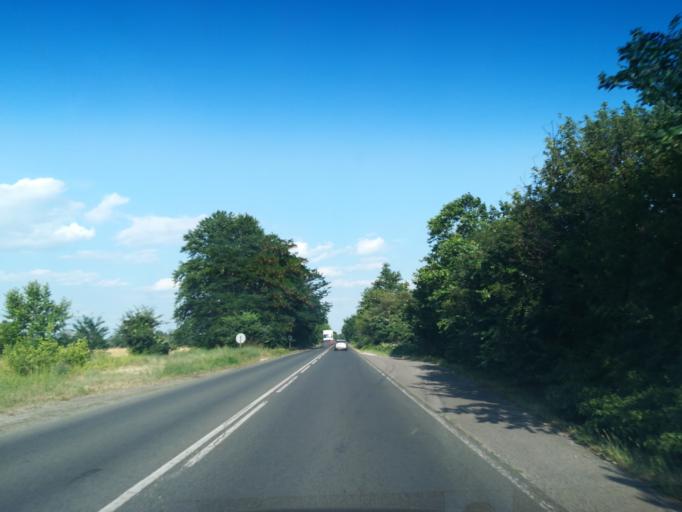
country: BG
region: Plovdiv
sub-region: Obshtina Plovdiv
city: Plovdiv
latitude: 42.1482
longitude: 24.8346
